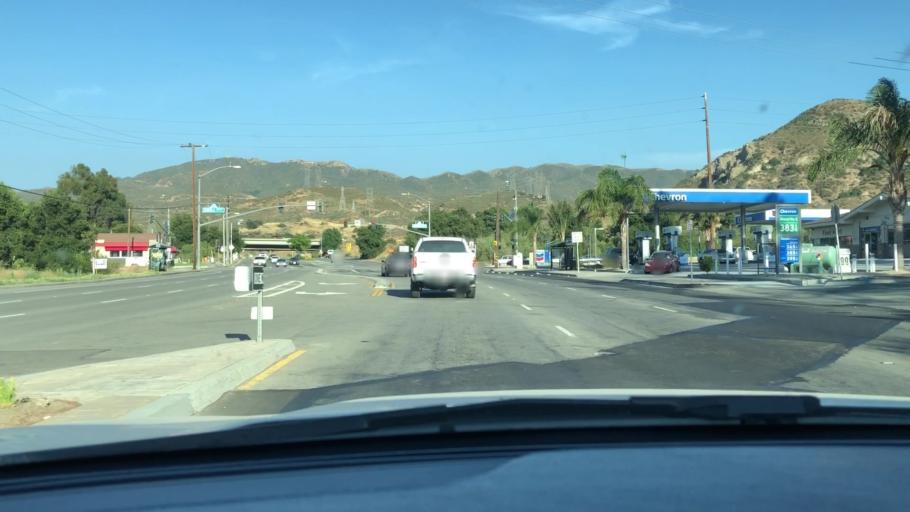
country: US
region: California
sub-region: Los Angeles County
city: Santa Clarita
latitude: 34.3663
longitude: -118.5075
